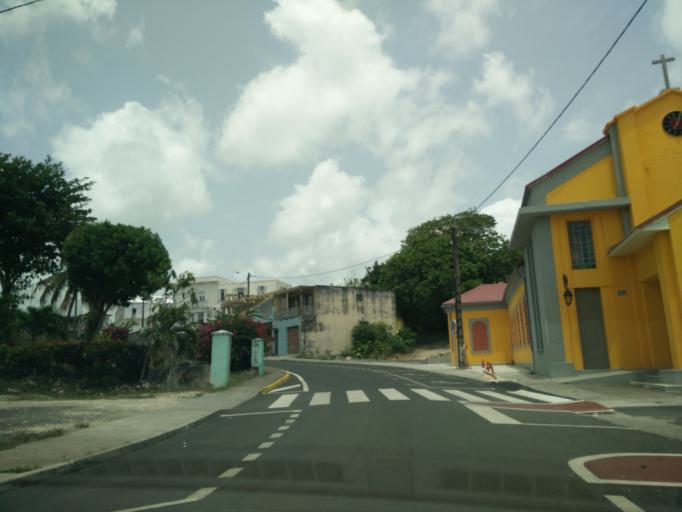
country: GP
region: Guadeloupe
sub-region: Guadeloupe
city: Anse-Bertrand
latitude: 16.4729
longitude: -61.5085
